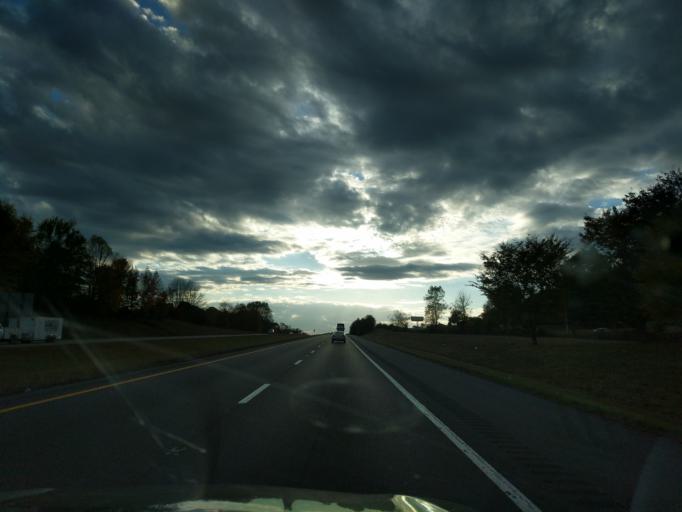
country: US
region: Tennessee
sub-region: Sullivan County
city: Walnut Hill
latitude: 36.5743
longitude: -82.2859
